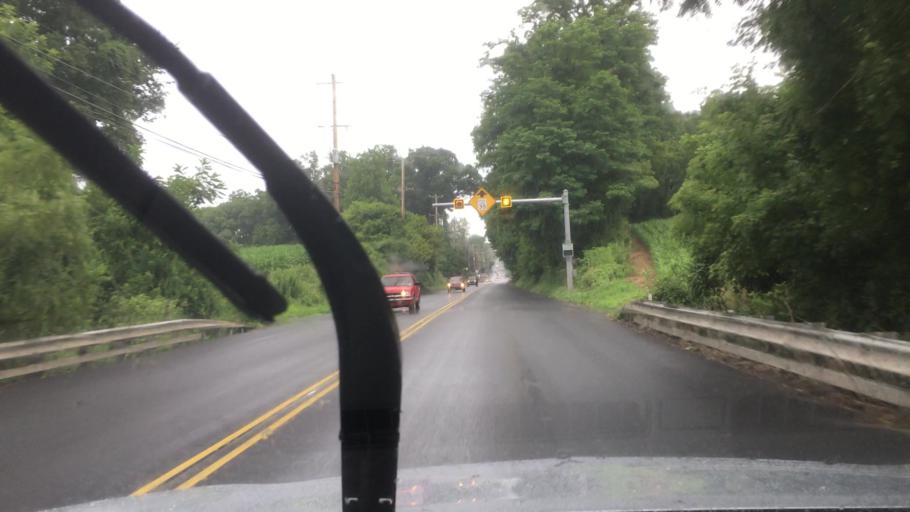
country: US
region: Pennsylvania
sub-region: Chester County
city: West Grove
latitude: 39.8574
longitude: -75.8313
